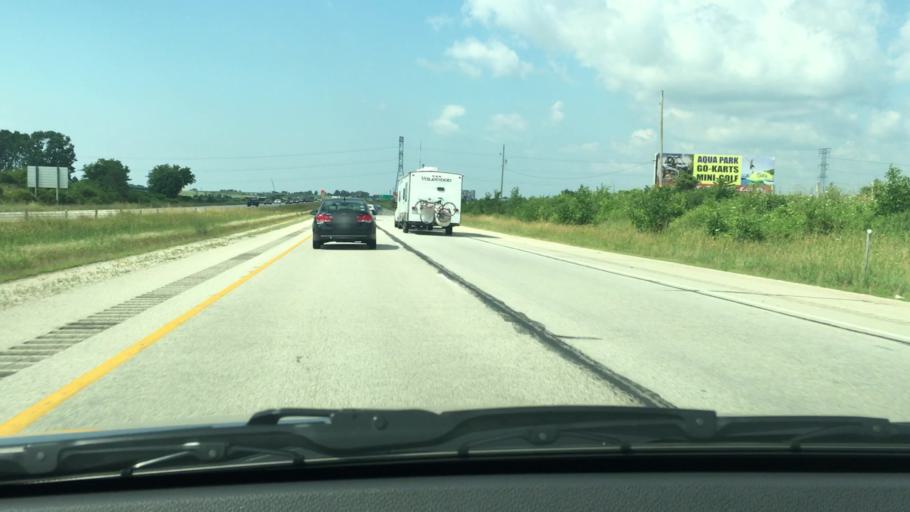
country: US
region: Wisconsin
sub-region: Fond du Lac County
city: Fond du Lac
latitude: 43.7212
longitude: -88.4422
